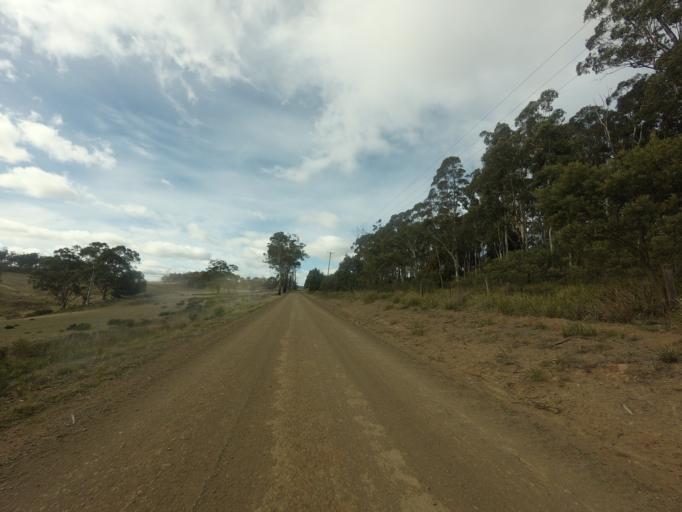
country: AU
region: Tasmania
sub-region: Brighton
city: Bridgewater
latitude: -42.3859
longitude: 147.4098
